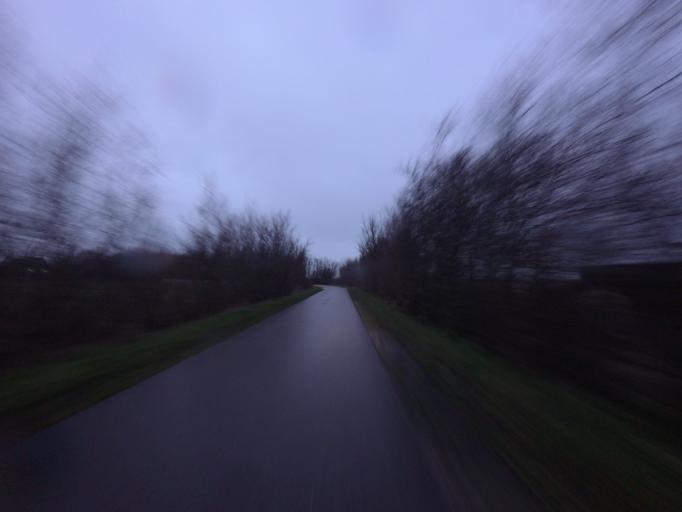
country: NL
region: North Holland
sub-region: Gemeente Texel
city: Den Burg
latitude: 53.0672
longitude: 4.7960
